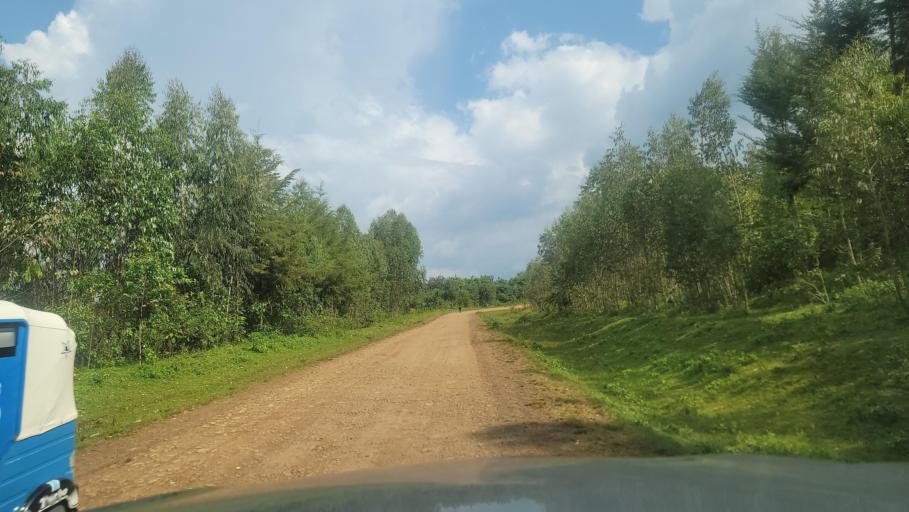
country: ET
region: Oromiya
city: Agaro
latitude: 7.7281
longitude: 36.2560
